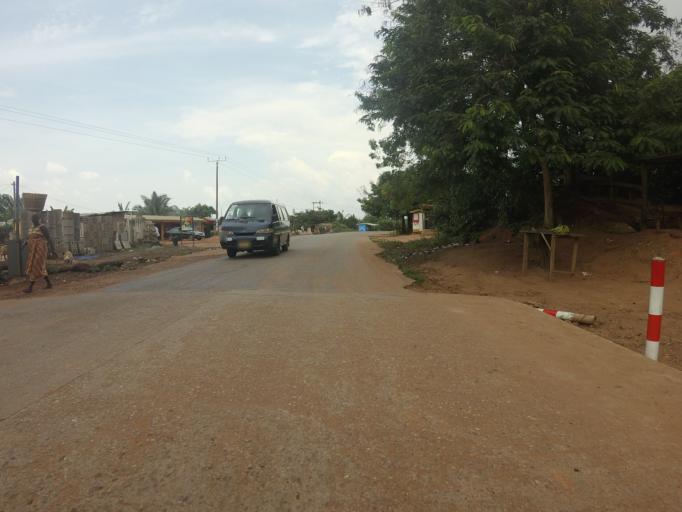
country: GH
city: Akropong
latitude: 5.9573
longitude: -0.1461
